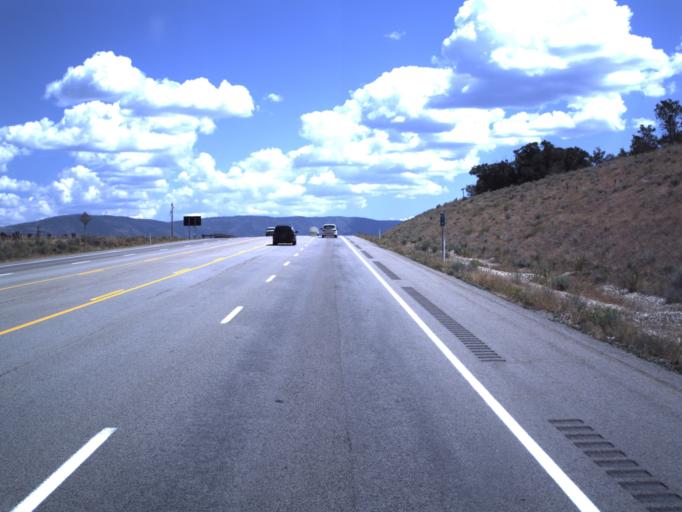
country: US
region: Utah
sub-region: Wasatch County
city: Midway
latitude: 40.4108
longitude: -111.5082
